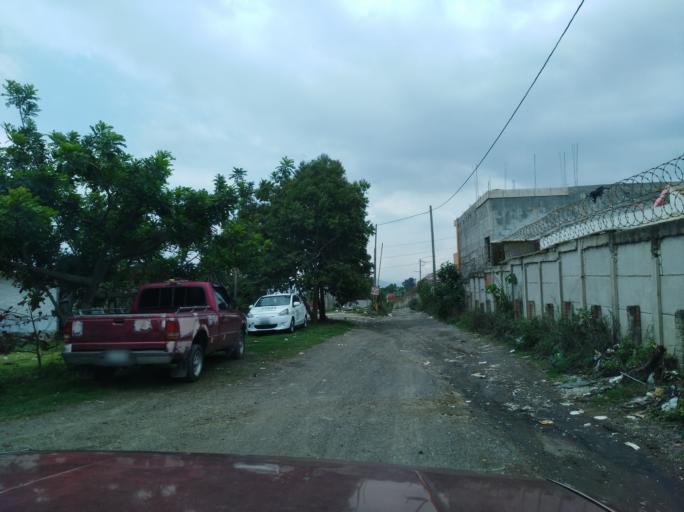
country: GT
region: Guatemala
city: Amatitlan
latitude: 14.5231
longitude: -90.6256
